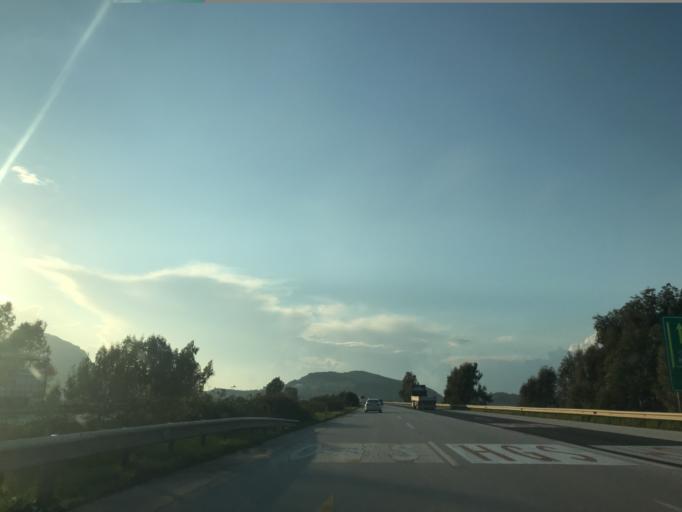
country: TR
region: Adana
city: Ceyhan
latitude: 36.9855
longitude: 35.7676
